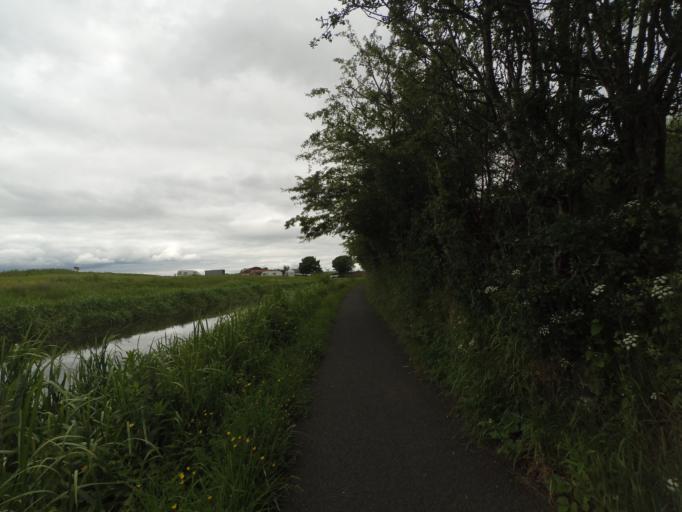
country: GB
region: Scotland
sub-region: West Lothian
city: Linlithgow
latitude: 55.9755
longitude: -3.5364
